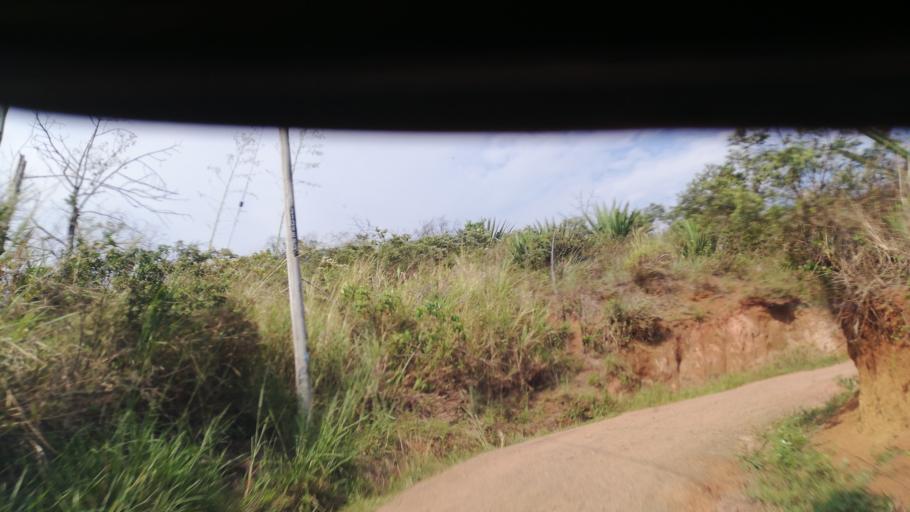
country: CO
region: Valle del Cauca
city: Cali
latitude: 3.4930
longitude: -76.5440
